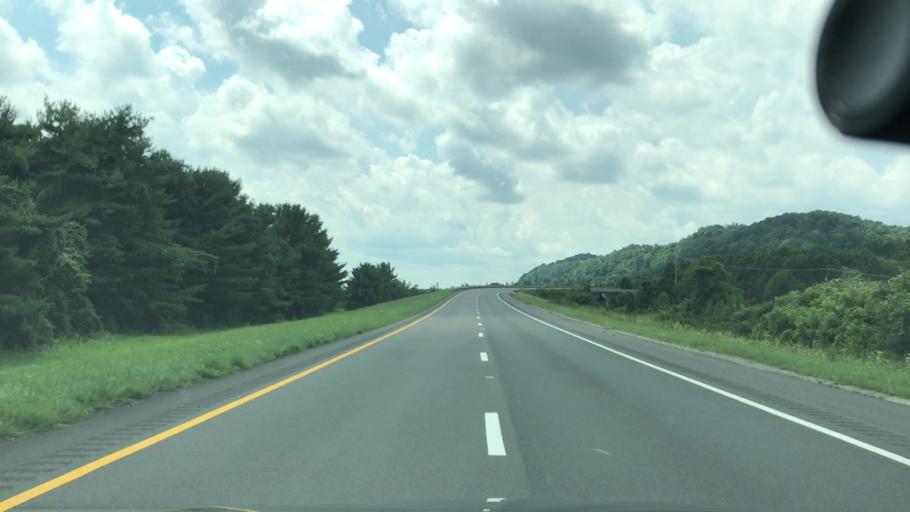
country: US
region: West Virginia
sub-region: Mason County
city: Point Pleasant
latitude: 38.8402
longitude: -82.1600
